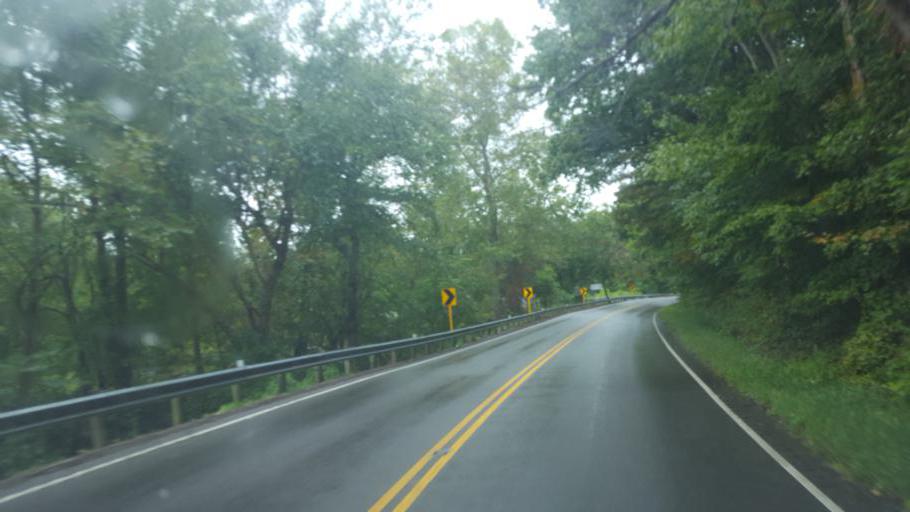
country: US
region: Ohio
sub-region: Jackson County
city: Oak Hill
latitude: 38.8120
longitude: -82.6742
